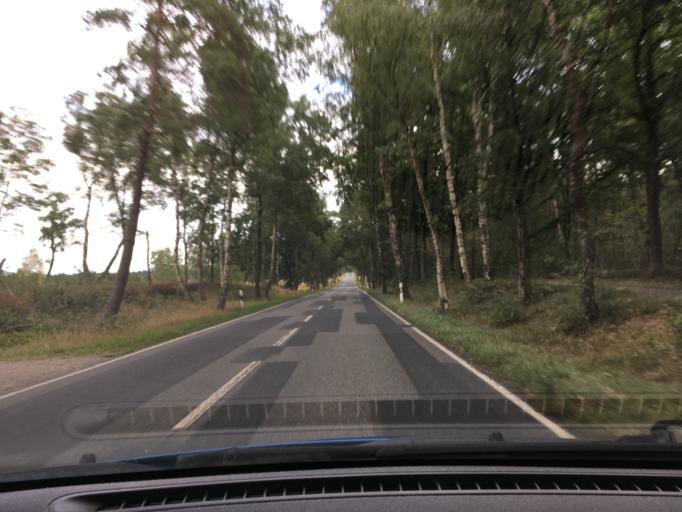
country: DE
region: Lower Saxony
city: Undeloh
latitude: 53.2213
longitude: 9.9362
